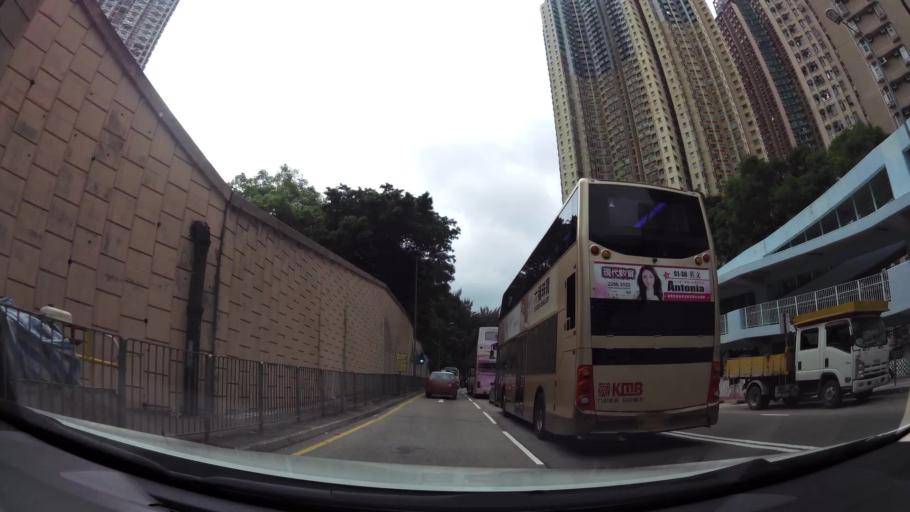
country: HK
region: Wong Tai Sin
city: Wong Tai Sin
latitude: 22.3428
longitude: 114.2013
